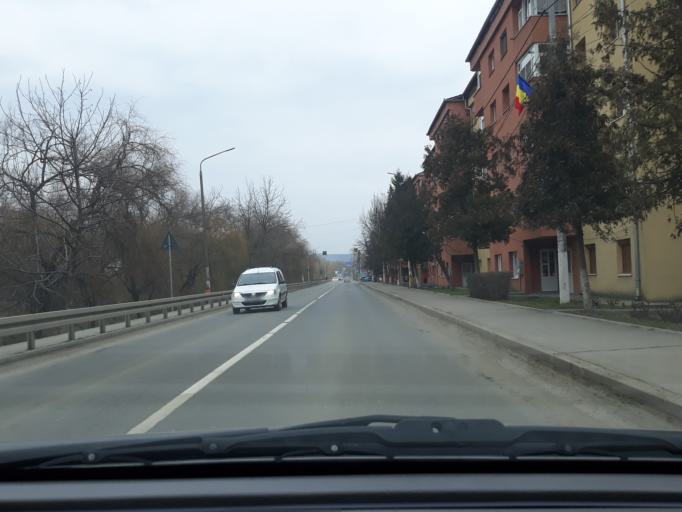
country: RO
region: Salaj
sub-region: Oras Simleu Silvaniei
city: Simleu Silvaniei
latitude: 47.2268
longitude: 22.7951
